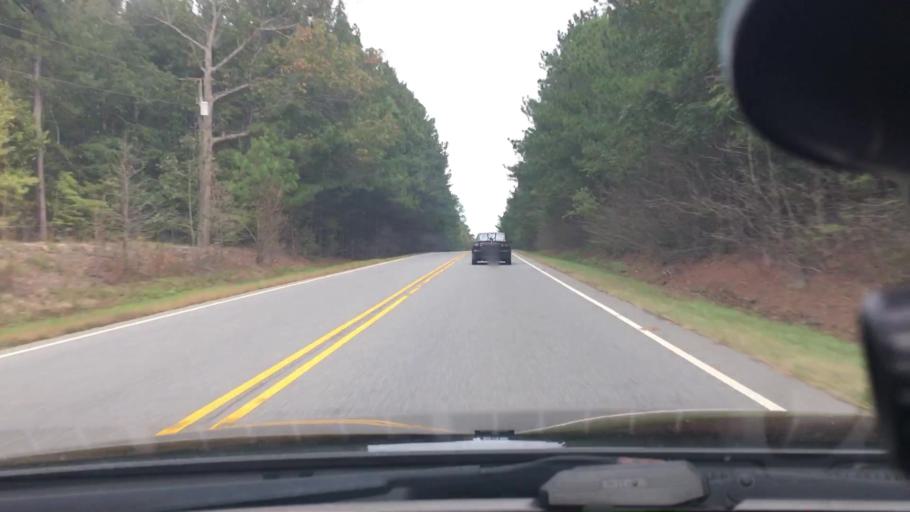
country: US
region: North Carolina
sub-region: Montgomery County
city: Biscoe
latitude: 35.3601
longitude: -79.7154
